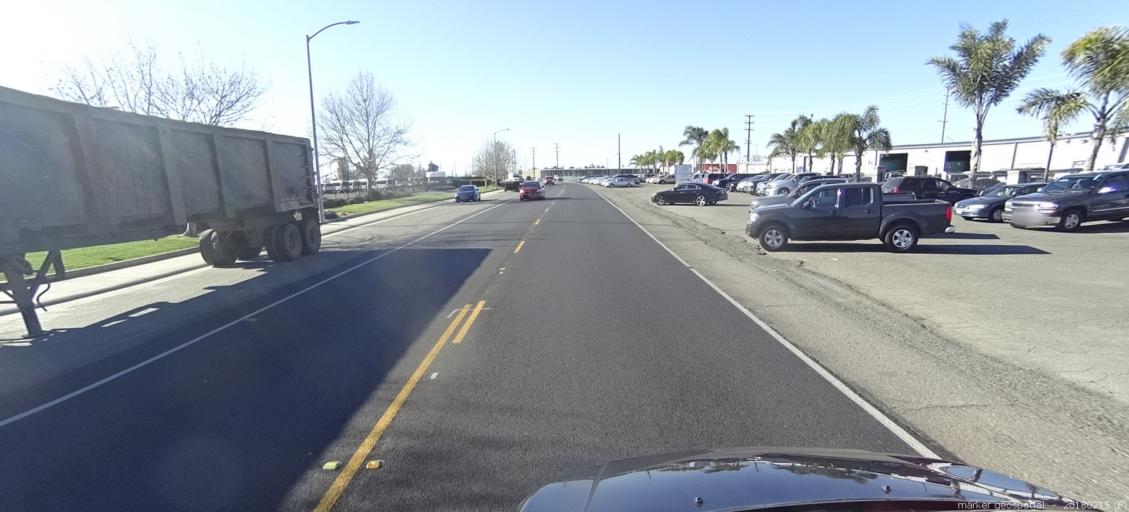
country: US
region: California
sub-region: Sacramento County
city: Rio Linda
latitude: 38.6845
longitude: -121.4768
